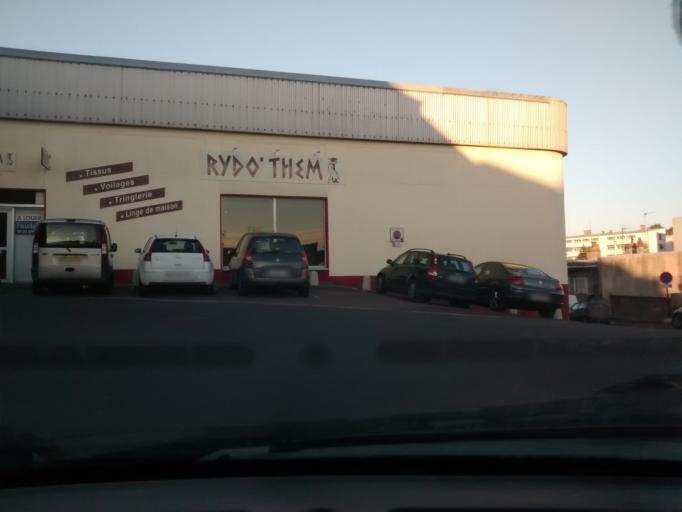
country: FR
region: Lower Normandy
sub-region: Departement de la Manche
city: Saint-Lo
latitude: 49.1139
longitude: -1.0887
